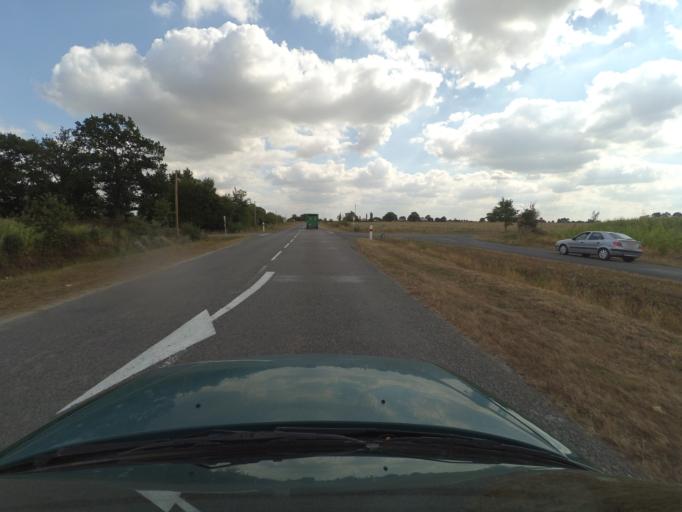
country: FR
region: Pays de la Loire
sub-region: Departement de la Loire-Atlantique
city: Aigrefeuille-sur-Maine
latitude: 47.0475
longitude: -1.4156
